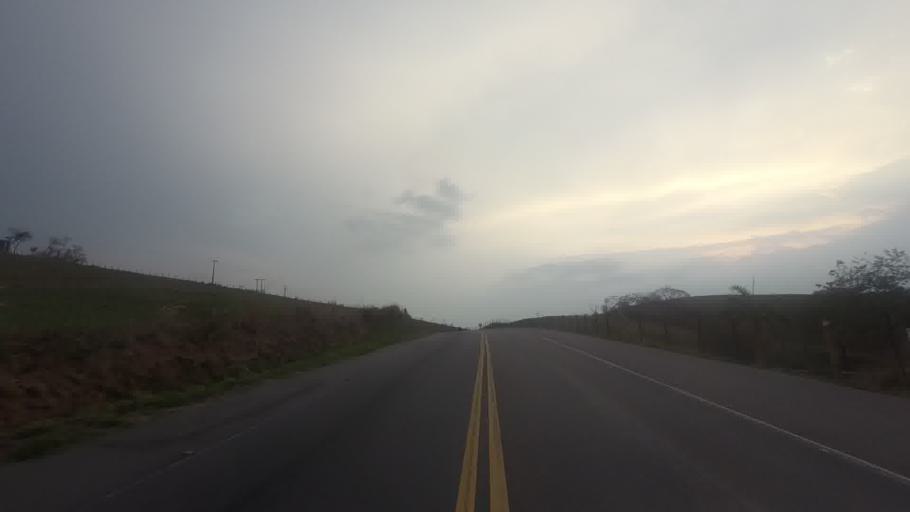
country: BR
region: Rio de Janeiro
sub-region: Carmo
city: Carmo
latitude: -21.8041
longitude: -42.5749
